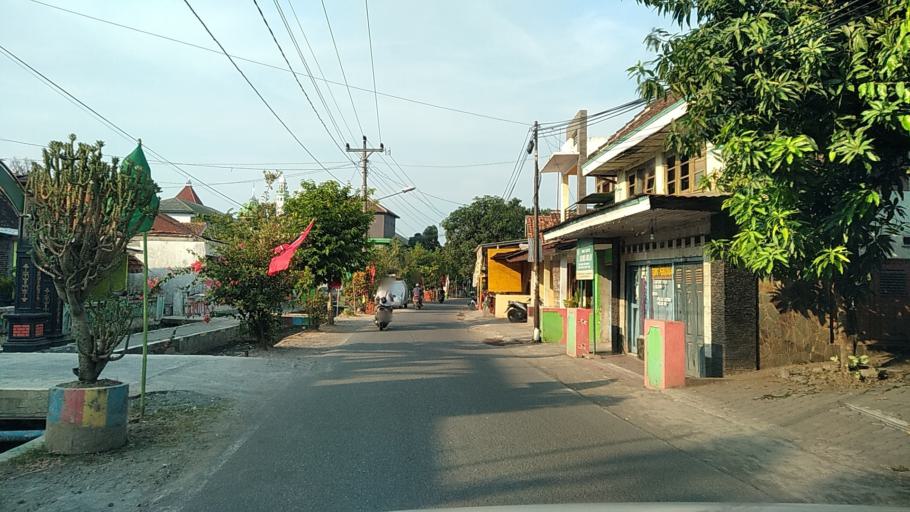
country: ID
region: Central Java
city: Semarang
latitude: -6.9723
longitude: 110.2963
